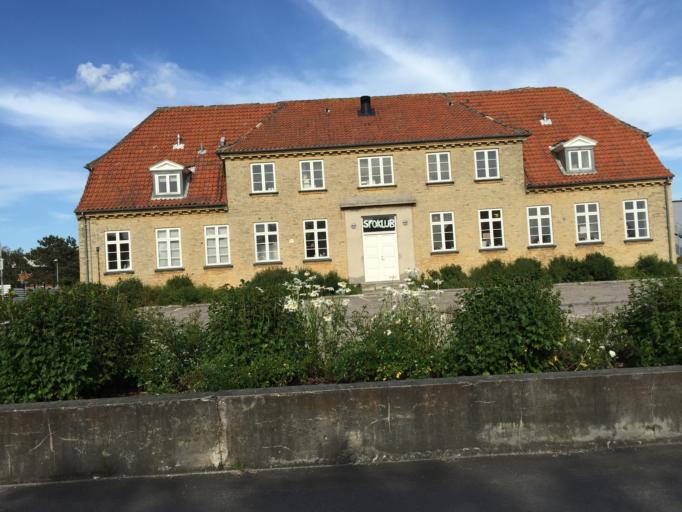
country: DK
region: Capital Region
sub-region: Halsnaes Kommune
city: Hundested
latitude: 55.9568
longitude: 11.8539
